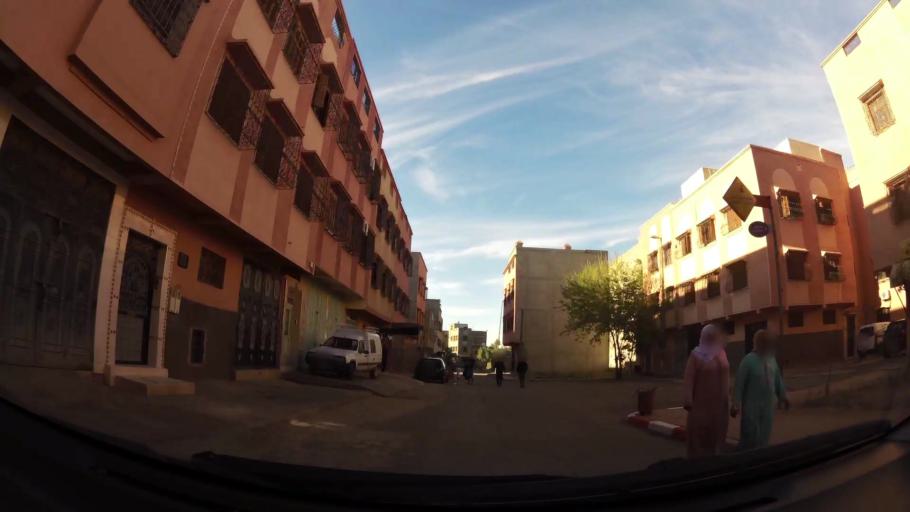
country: MA
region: Marrakech-Tensift-Al Haouz
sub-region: Marrakech
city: Marrakesh
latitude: 31.6160
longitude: -8.0690
